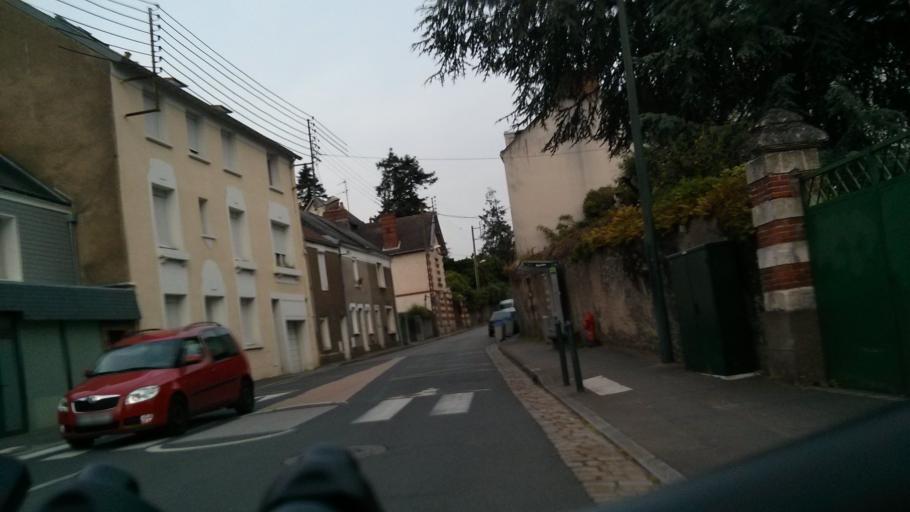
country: FR
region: Pays de la Loire
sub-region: Departement de la Loire-Atlantique
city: Reze
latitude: 47.1917
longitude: -1.5350
